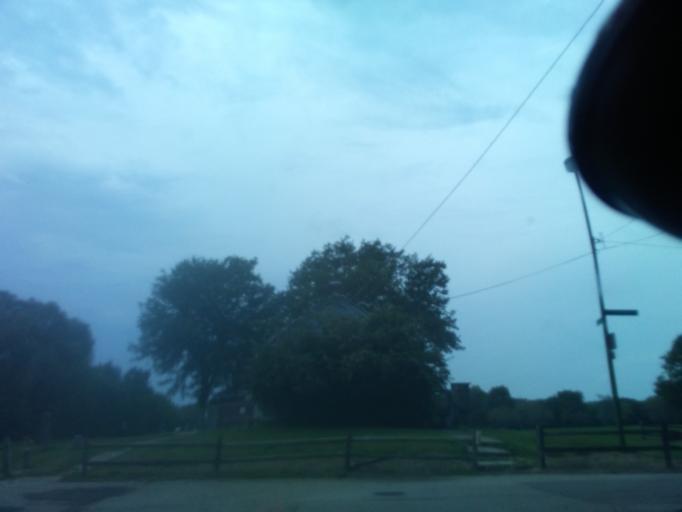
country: US
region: Illinois
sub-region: Cook County
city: Lincolnwood
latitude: 41.9881
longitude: -87.7568
